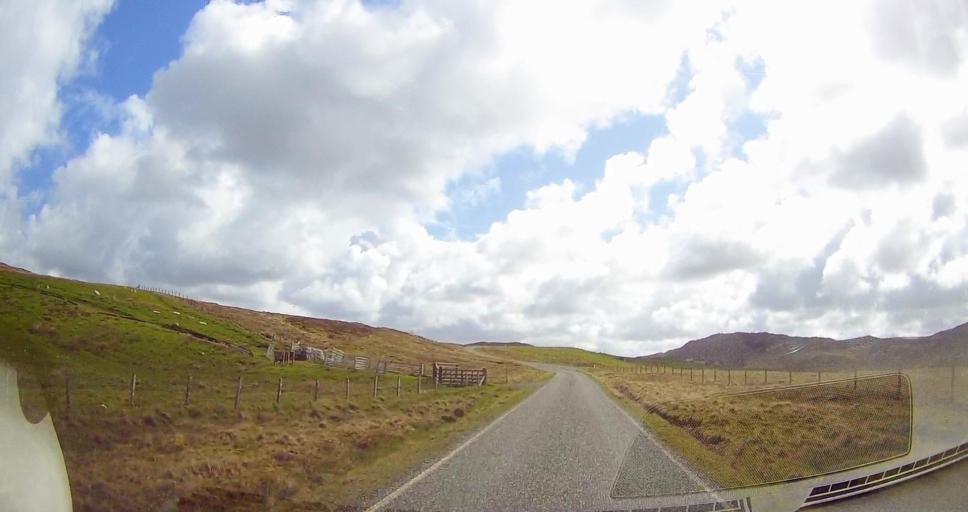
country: GB
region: Scotland
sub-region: Shetland Islands
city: Lerwick
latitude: 60.5646
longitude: -1.3338
